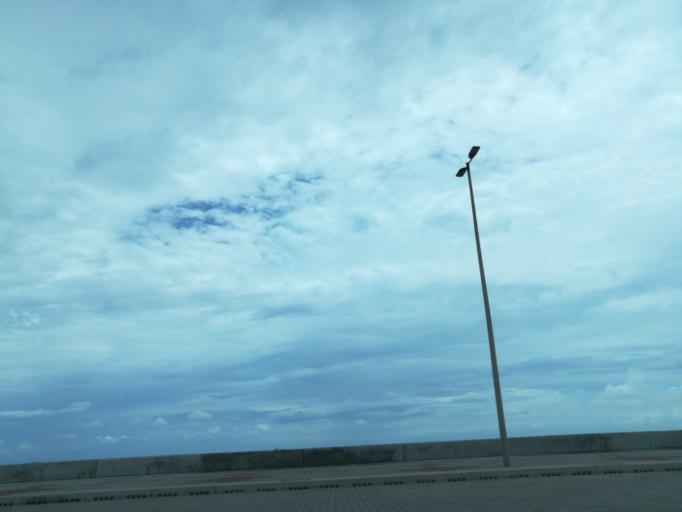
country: NG
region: Lagos
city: Ikoyi
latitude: 6.4064
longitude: 3.4205
